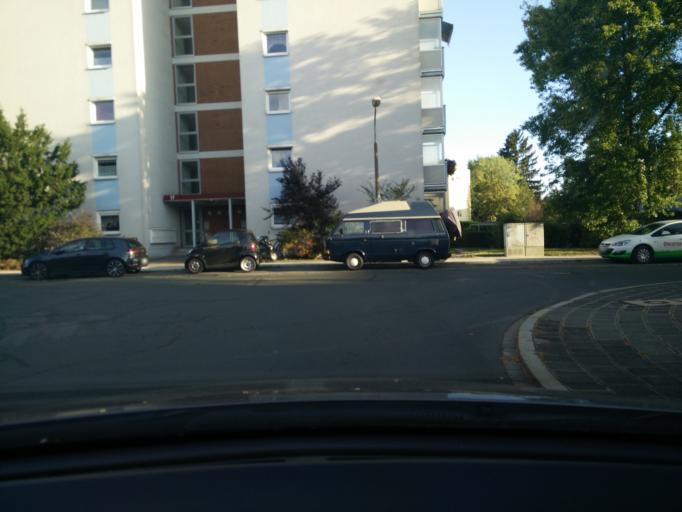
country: DE
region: Bavaria
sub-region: Regierungsbezirk Mittelfranken
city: Nuernberg
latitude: 49.4066
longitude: 11.0845
